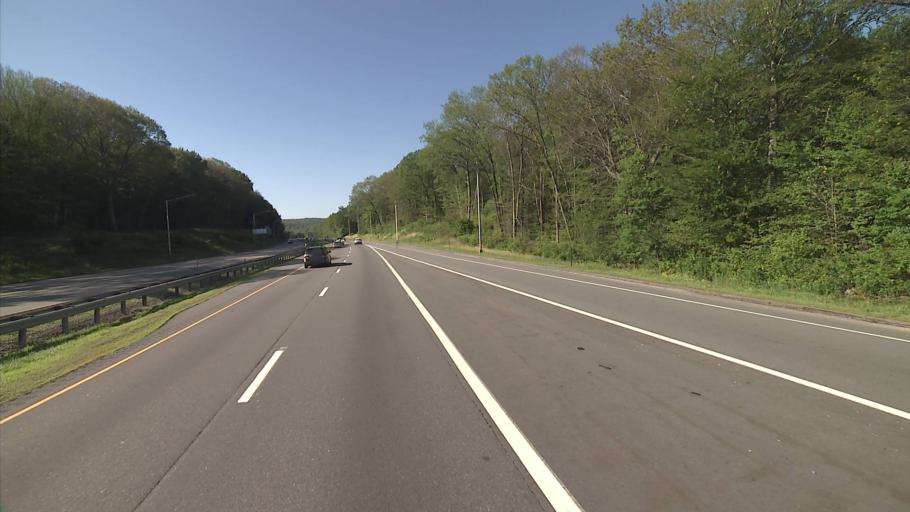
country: US
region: Connecticut
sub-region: New London County
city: Oxoboxo River
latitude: 41.4718
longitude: -72.1168
